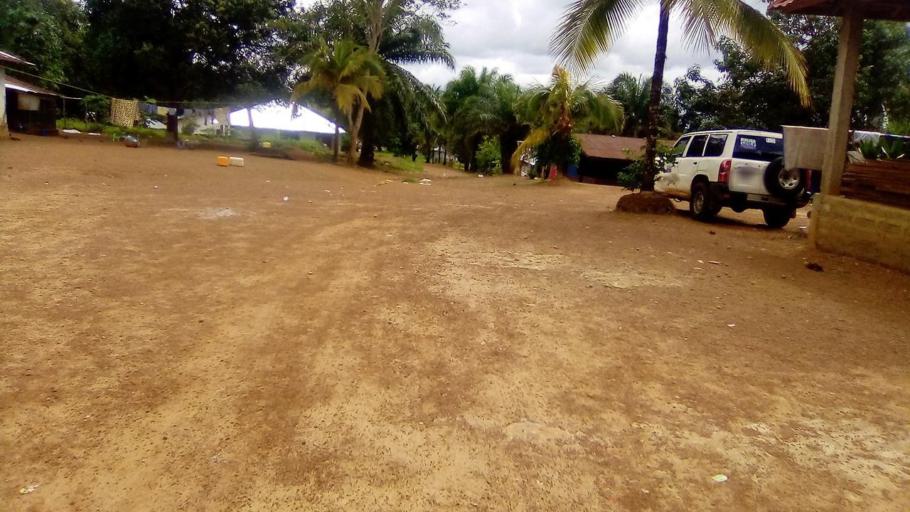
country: SL
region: Southern Province
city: Pujehun
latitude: 7.3614
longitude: -11.7253
